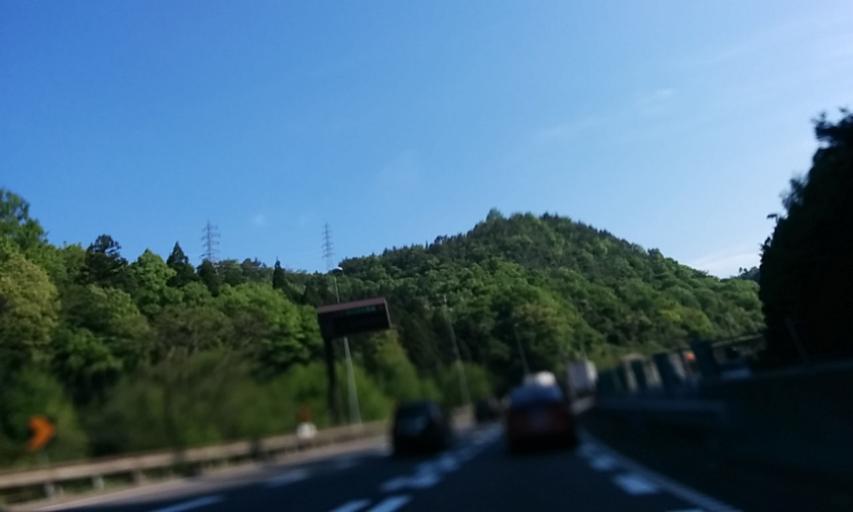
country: JP
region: Shiga Prefecture
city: Hikone
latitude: 35.2948
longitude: 136.2977
